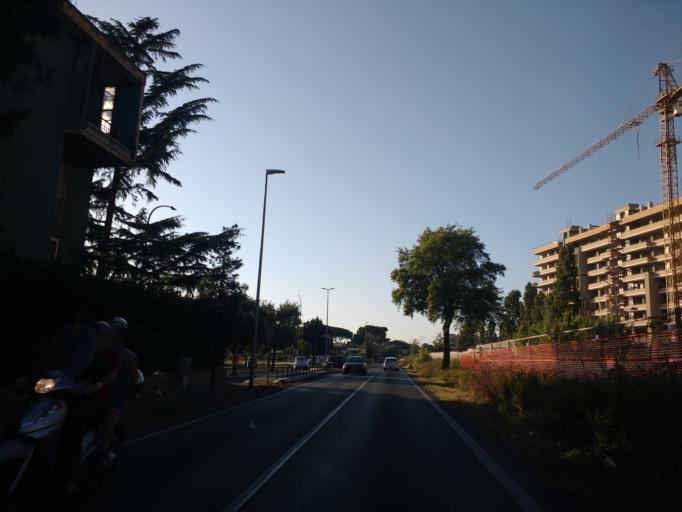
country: IT
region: Latium
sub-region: Citta metropolitana di Roma Capitale
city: Vitinia
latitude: 41.7718
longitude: 12.3727
